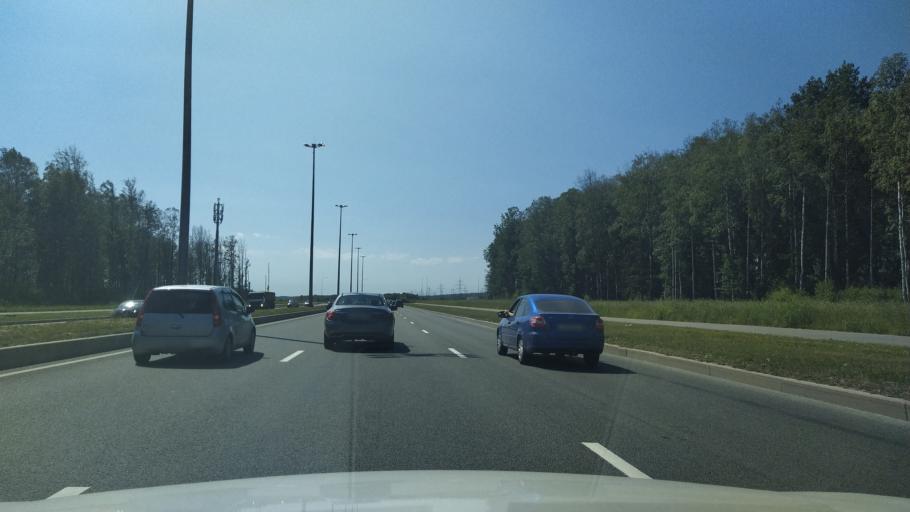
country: RU
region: St.-Petersburg
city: Levashovo
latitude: 60.0638
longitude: 30.2004
